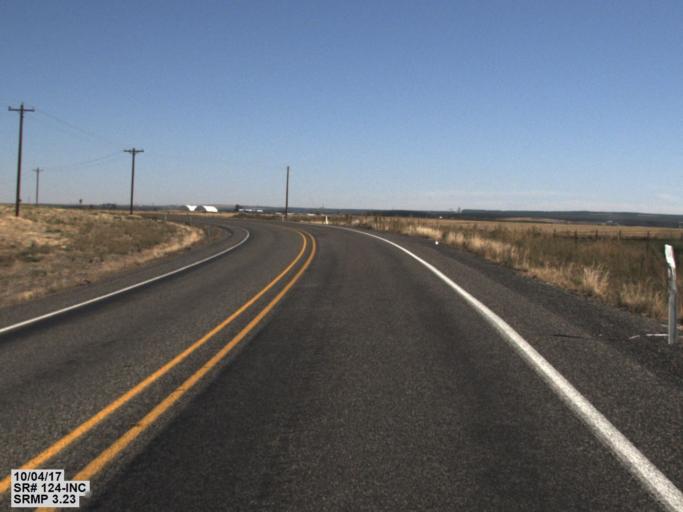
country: US
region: Washington
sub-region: Walla Walla County
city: Burbank
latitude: 46.2118
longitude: -118.9472
